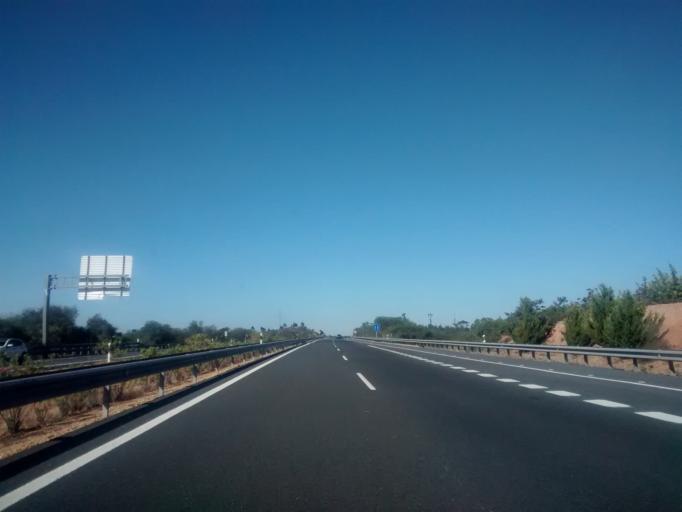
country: ES
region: Andalusia
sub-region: Provincia de Huelva
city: Villablanca
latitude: 37.2482
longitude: -7.3423
